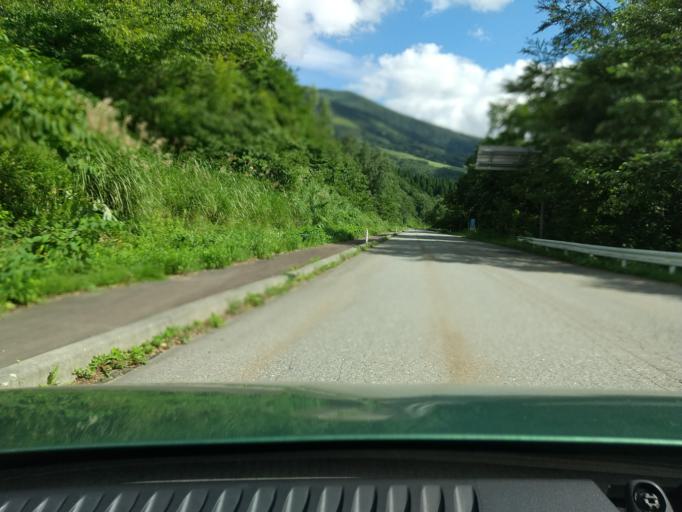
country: JP
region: Iwate
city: Shizukuishi
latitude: 39.7770
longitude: 140.7623
